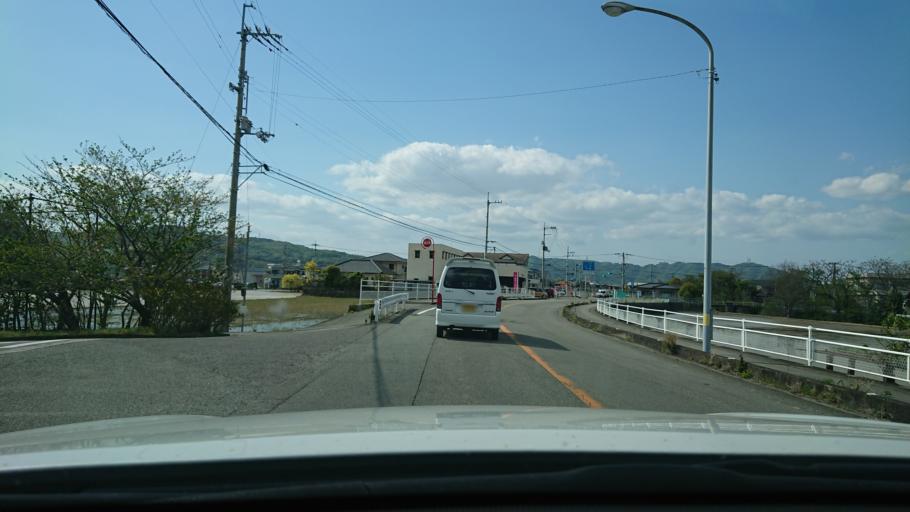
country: JP
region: Tokushima
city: Komatsushimacho
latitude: 34.0216
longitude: 134.5515
